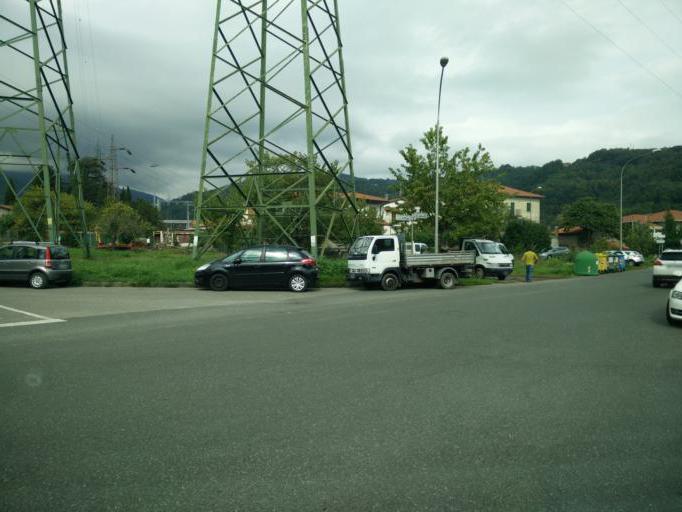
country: IT
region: Tuscany
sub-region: Provincia di Massa-Carrara
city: Pontremoli
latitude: 44.3786
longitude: 9.8748
